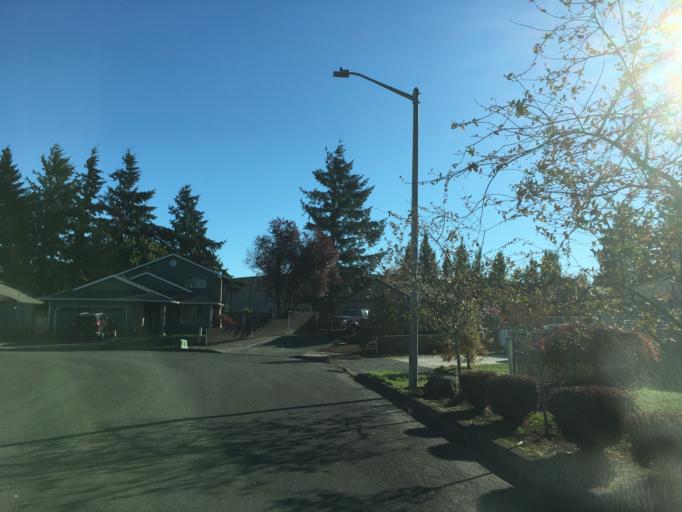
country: US
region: Oregon
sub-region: Multnomah County
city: Gresham
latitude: 45.5019
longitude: -122.4095
